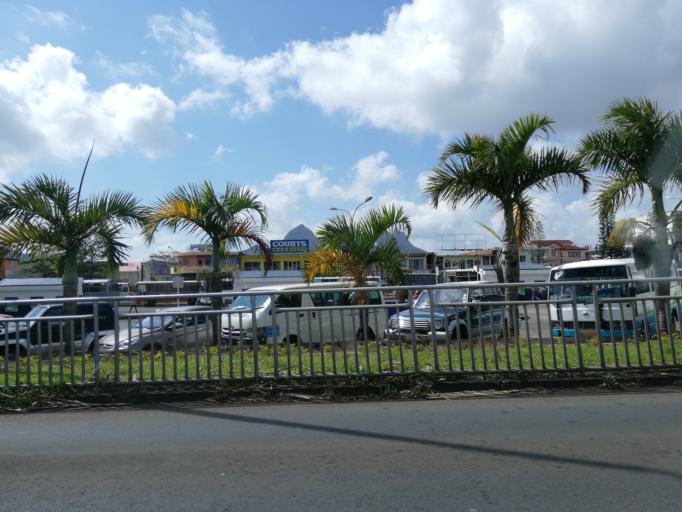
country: MU
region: Moka
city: Verdun
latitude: -20.2257
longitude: 57.5404
